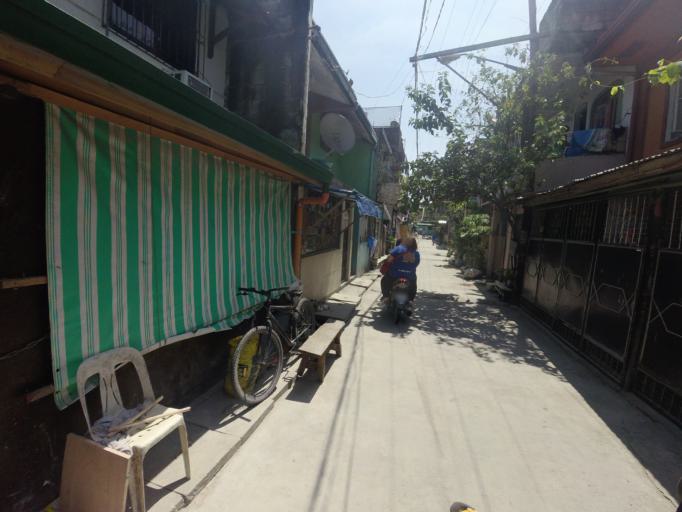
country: PH
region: Calabarzon
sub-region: Province of Rizal
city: Taytay
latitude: 14.5426
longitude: 121.1087
